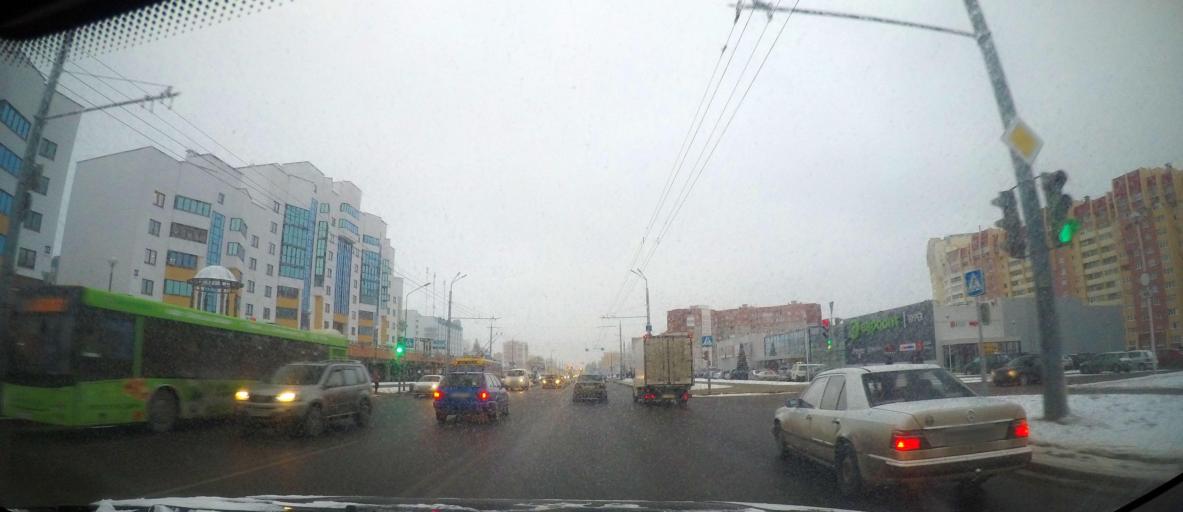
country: BY
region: Grodnenskaya
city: Hrodna
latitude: 53.6537
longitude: 23.8505
